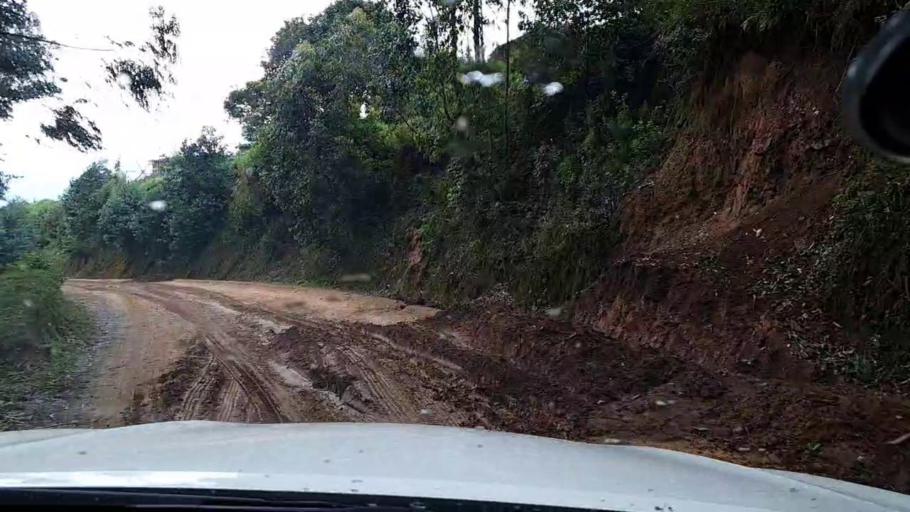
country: RW
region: Western Province
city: Kibuye
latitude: -2.2518
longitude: 29.3452
